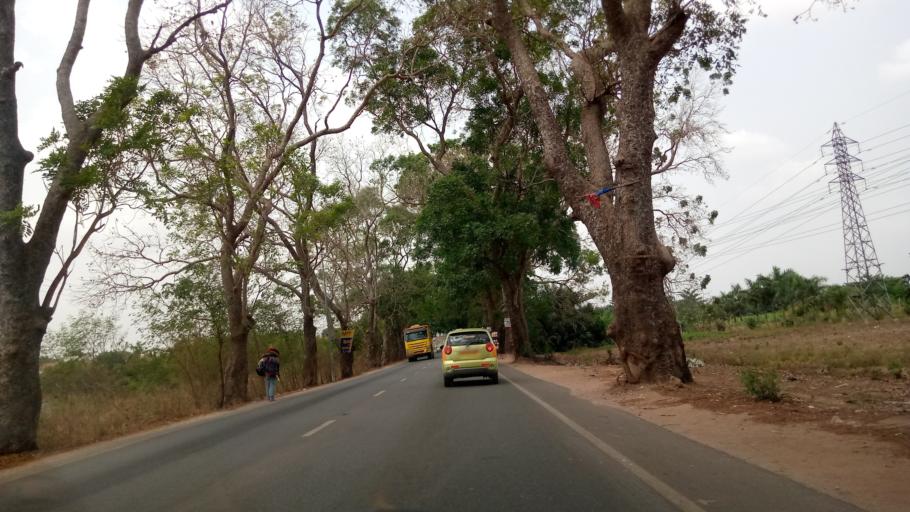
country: GH
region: Greater Accra
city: Dome
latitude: 5.6677
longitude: -0.2262
